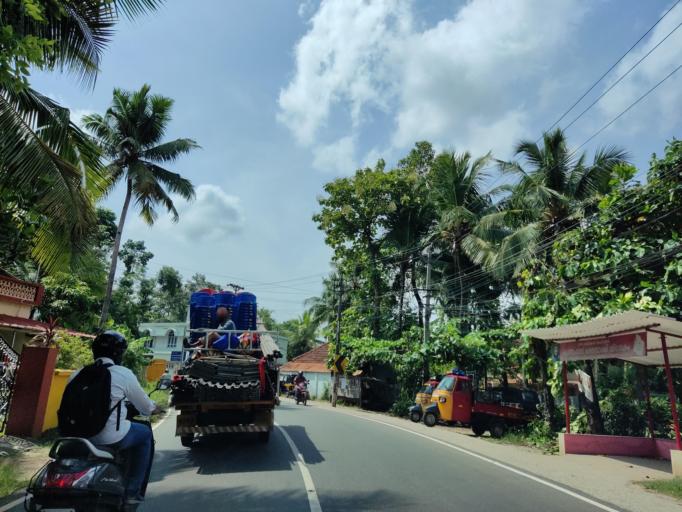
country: IN
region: Kerala
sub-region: Alappuzha
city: Mavelikara
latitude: 9.2672
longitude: 76.5407
